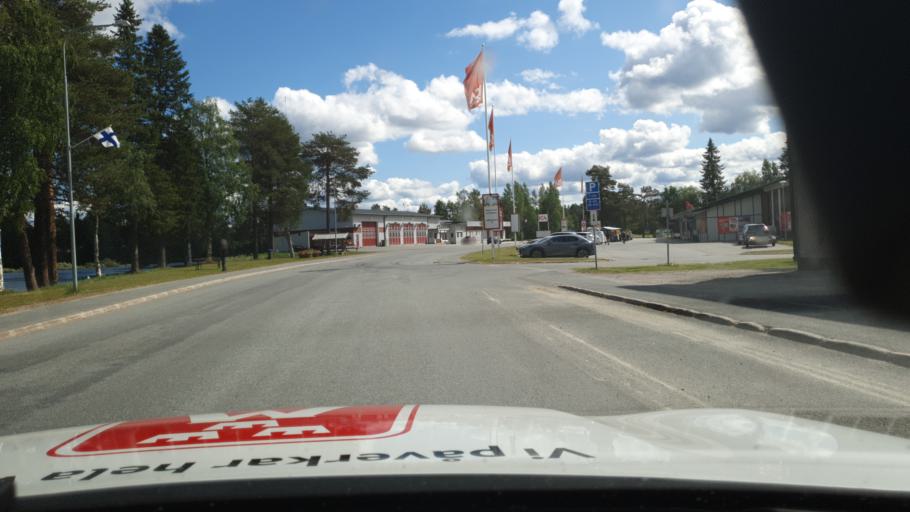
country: SE
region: Vaesterbotten
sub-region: Sorsele Kommun
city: Sorsele
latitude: 65.5374
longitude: 17.5291
